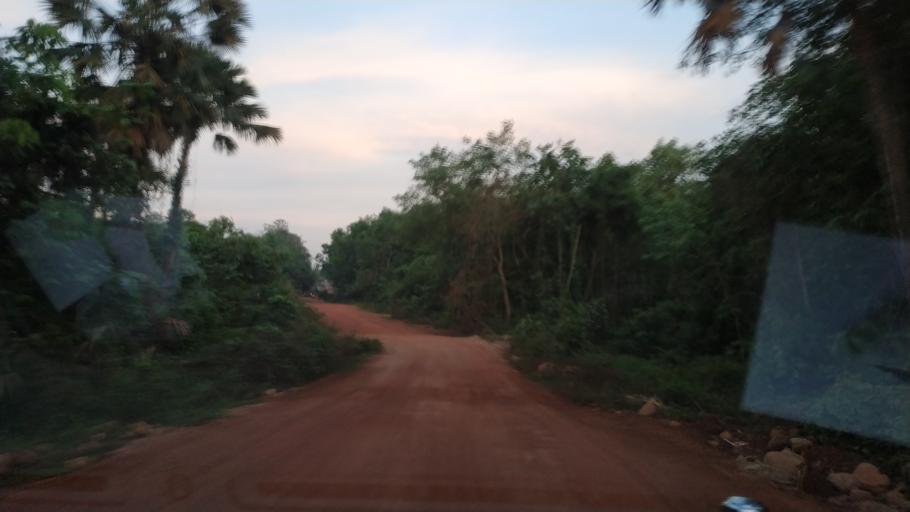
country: MM
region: Mon
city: Kyaikto
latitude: 17.4250
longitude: 97.0455
